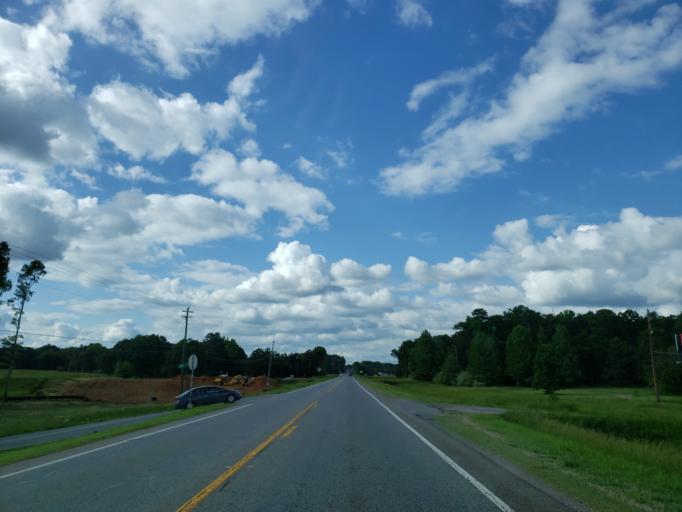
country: US
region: Georgia
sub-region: Bartow County
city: Cartersville
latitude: 34.2362
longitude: -84.8565
